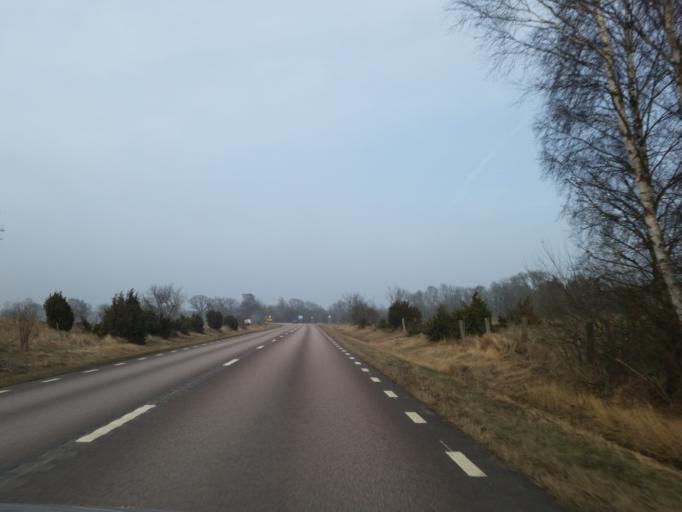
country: SE
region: Kalmar
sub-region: Borgholms Kommun
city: Borgholm
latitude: 57.1422
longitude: 17.0006
